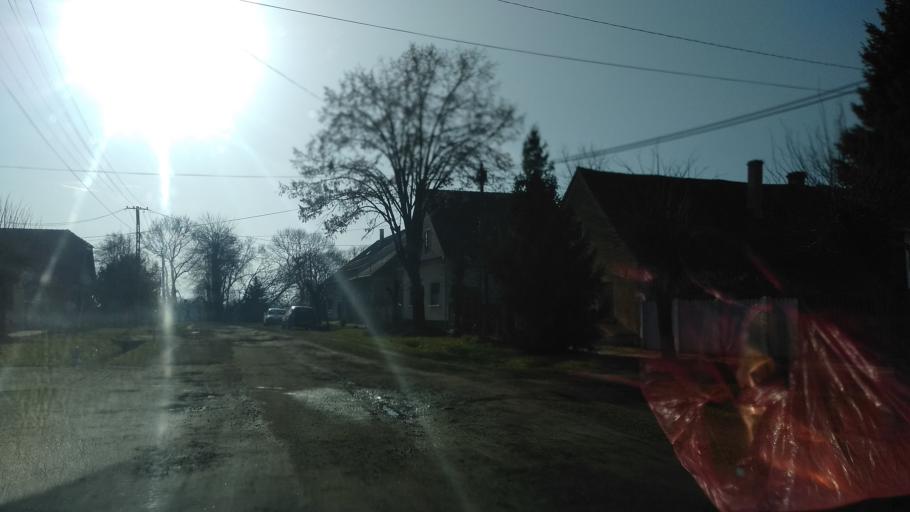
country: HU
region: Somogy
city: Barcs
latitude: 45.9599
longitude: 17.4821
